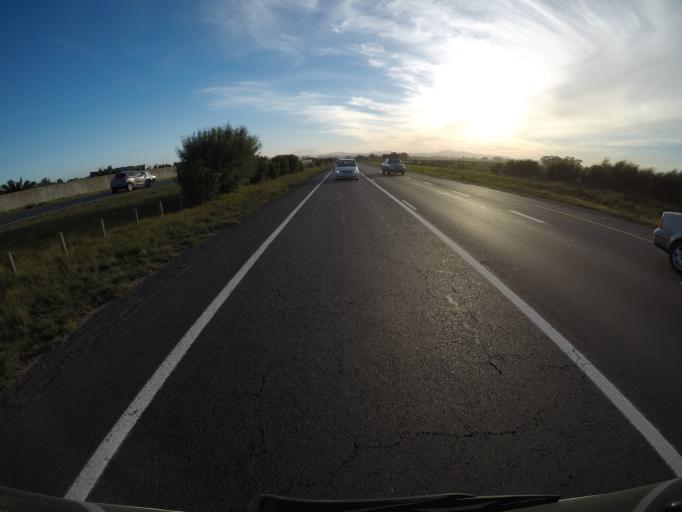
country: ZA
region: Western Cape
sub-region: City of Cape Town
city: Kraaifontein
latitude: -33.8288
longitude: 18.7593
